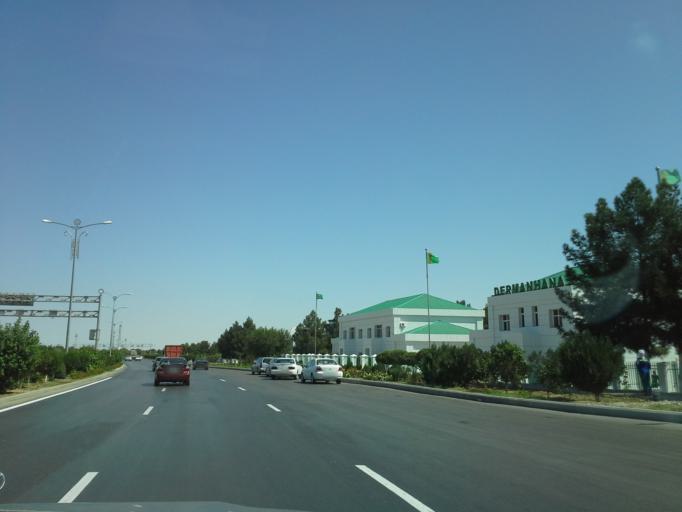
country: TM
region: Ahal
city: Annau
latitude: 37.9116
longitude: 58.4895
